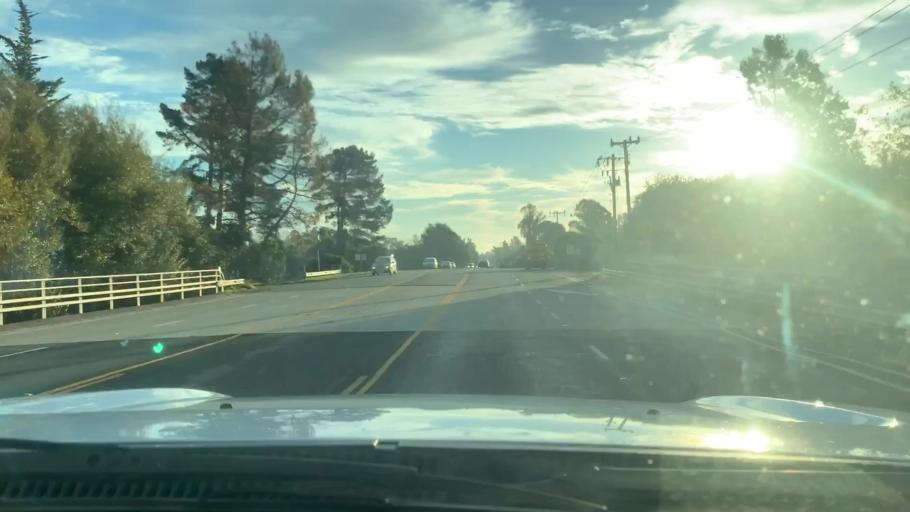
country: US
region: California
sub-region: San Luis Obispo County
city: Los Osos
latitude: 35.3061
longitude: -120.8119
